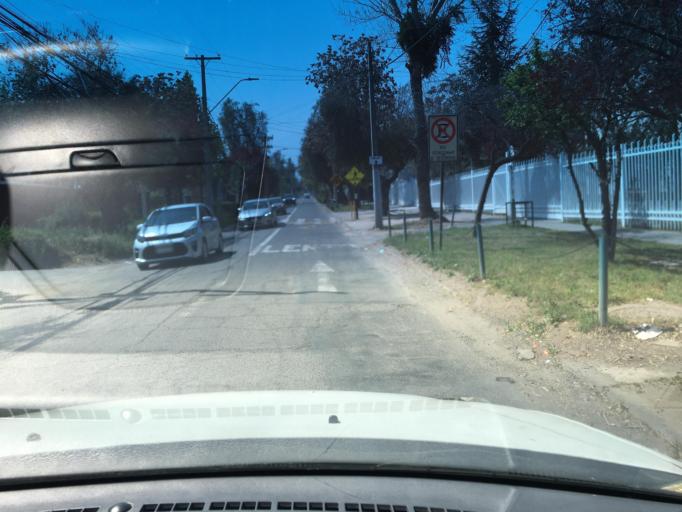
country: CL
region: Santiago Metropolitan
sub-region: Provincia de Santiago
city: Villa Presidente Frei, Nunoa, Santiago, Chile
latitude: -33.5216
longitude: -70.5684
